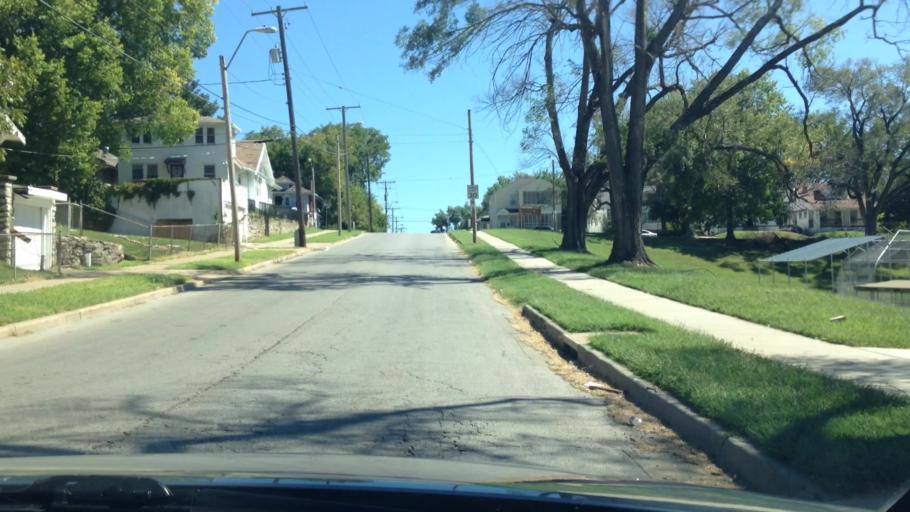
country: US
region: Missouri
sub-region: Jackson County
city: Kansas City
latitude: 39.0481
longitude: -94.5505
